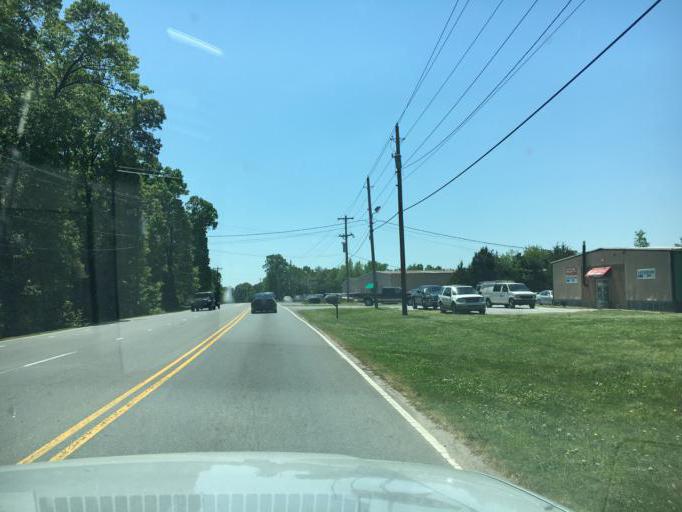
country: US
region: North Carolina
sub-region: Cleveland County
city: Shelby
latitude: 35.2567
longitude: -81.5644
